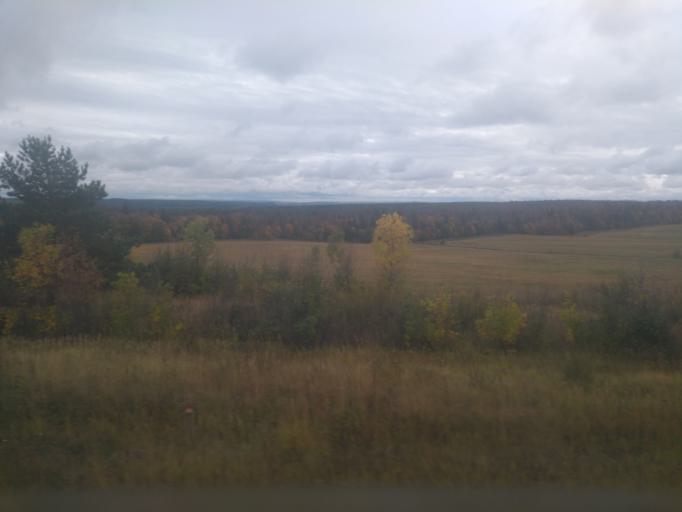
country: RU
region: Udmurtiya
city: Alnashi
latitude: 56.1541
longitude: 52.5816
